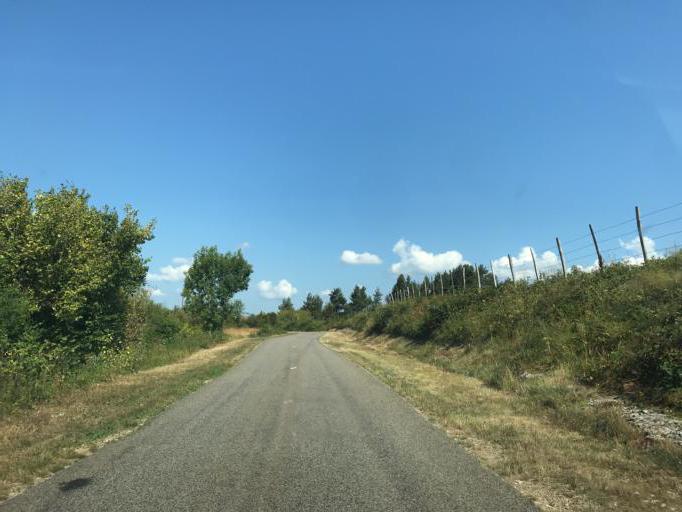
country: FR
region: Franche-Comte
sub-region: Departement du Jura
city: Moirans-en-Montagne
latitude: 46.4653
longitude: 5.7238
